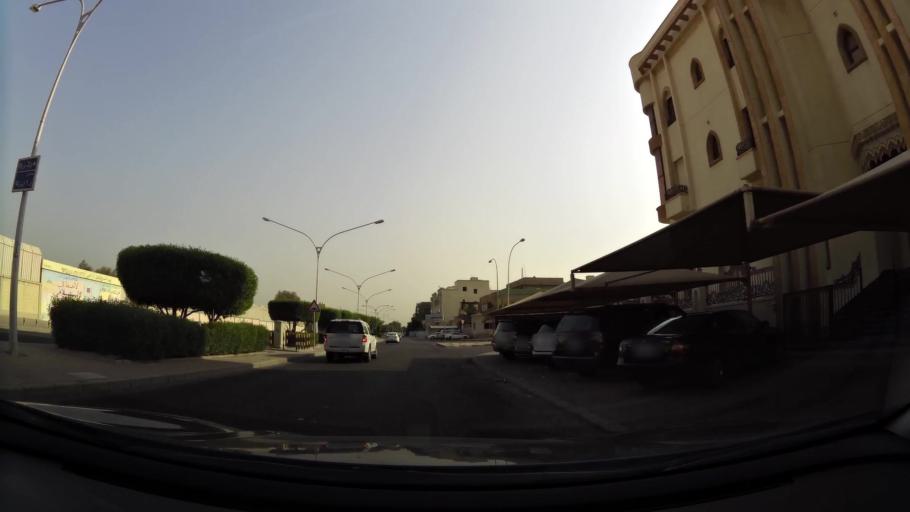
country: KW
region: Al Ahmadi
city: Al Manqaf
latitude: 29.0996
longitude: 48.1052
